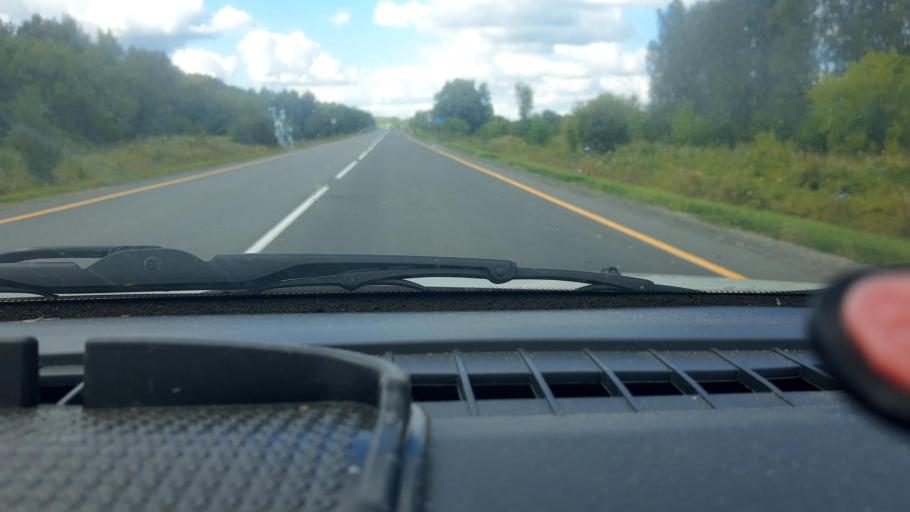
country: RU
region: Nizjnij Novgorod
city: Lukoyanov
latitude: 55.0536
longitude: 44.3722
